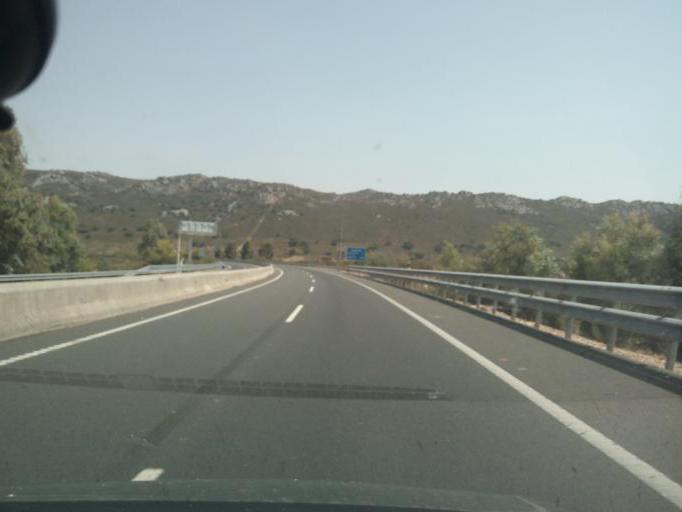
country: ES
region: Extremadura
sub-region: Provincia de Caceres
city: Higuera
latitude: 39.6997
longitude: -5.6915
